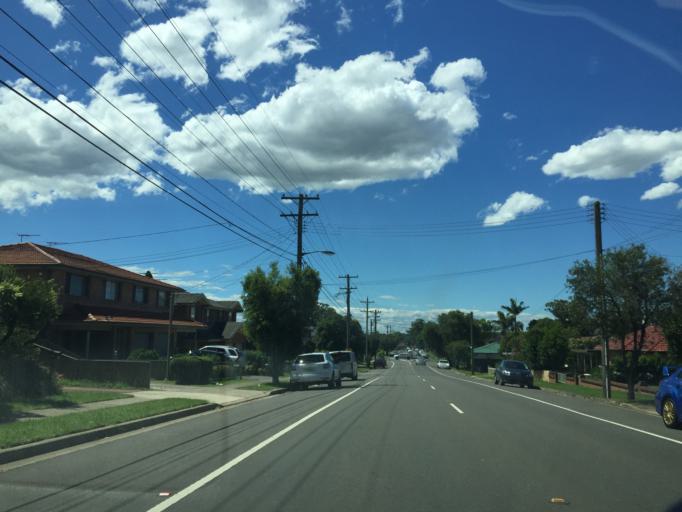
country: AU
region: New South Wales
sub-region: Blacktown
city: Blacktown
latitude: -33.7740
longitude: 150.8957
